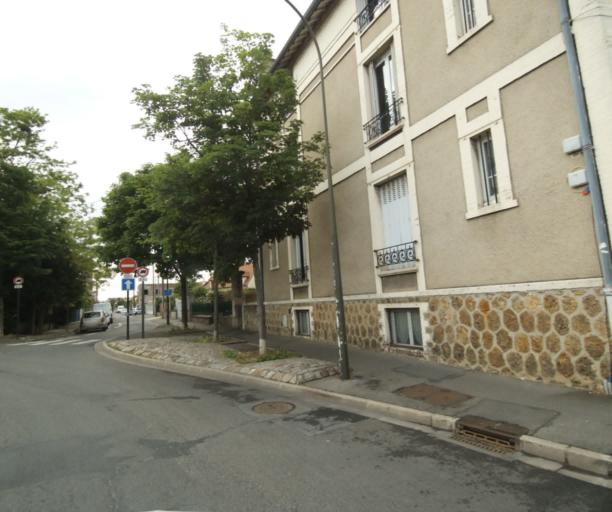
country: FR
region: Ile-de-France
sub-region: Departement du Val-d'Oise
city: Argenteuil
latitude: 48.9479
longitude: 2.2419
